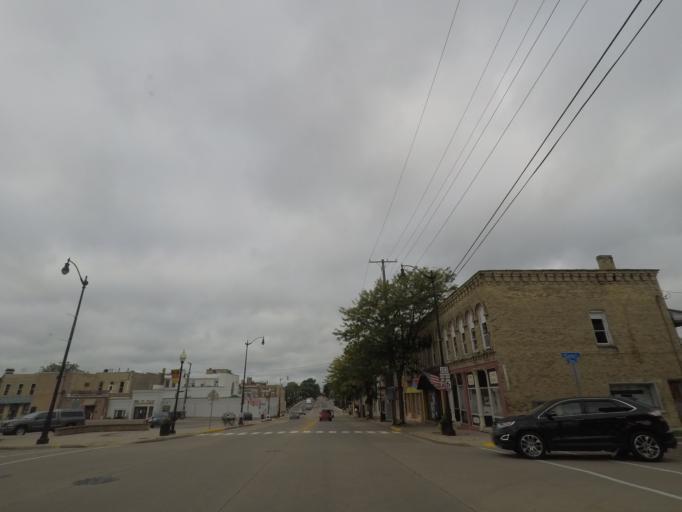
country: US
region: Wisconsin
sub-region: Jefferson County
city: Jefferson
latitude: 43.0053
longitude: -88.8057
